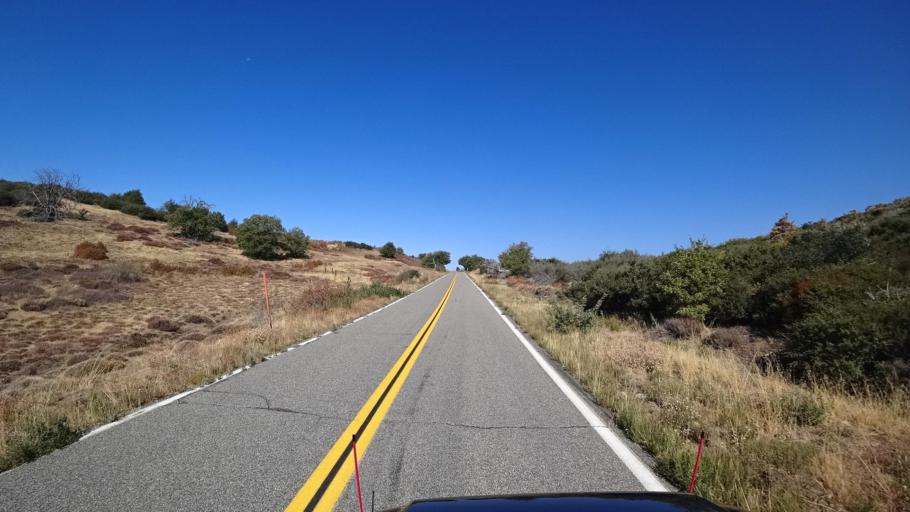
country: US
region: California
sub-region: San Diego County
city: Pine Valley
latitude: 32.9432
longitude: -116.4922
